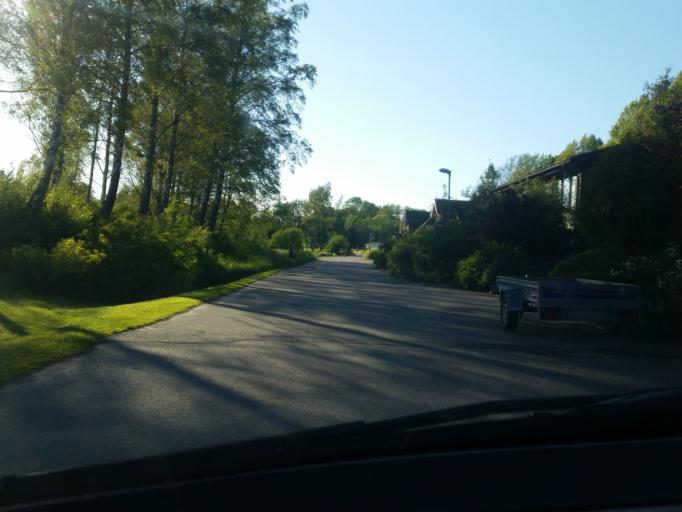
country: SE
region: Vaestra Goetaland
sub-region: Fargelanda Kommun
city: Faergelanda
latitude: 58.5145
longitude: 11.9805
